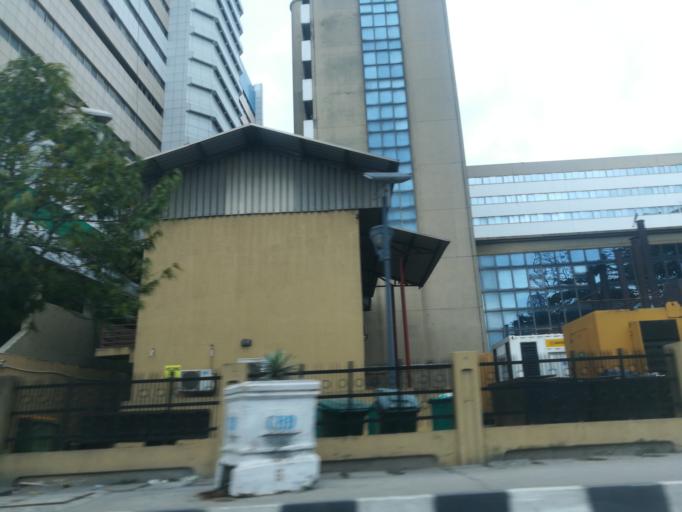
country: NG
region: Lagos
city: Lagos
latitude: 6.4496
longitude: 3.3923
